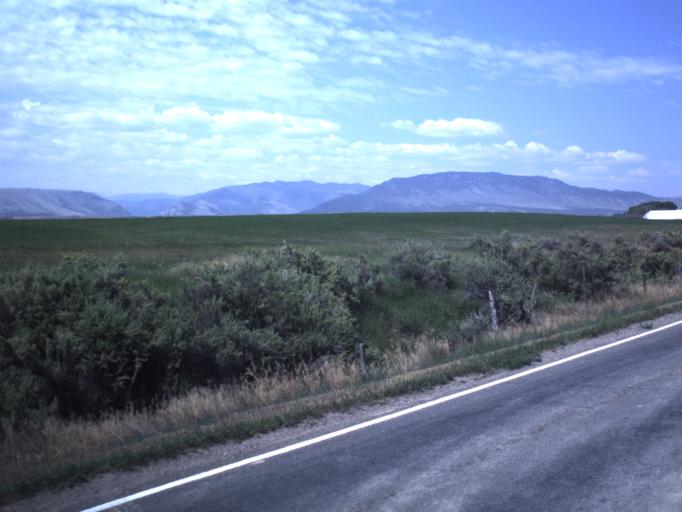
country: US
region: Utah
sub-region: Daggett County
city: Manila
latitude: 40.9886
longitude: -109.7045
